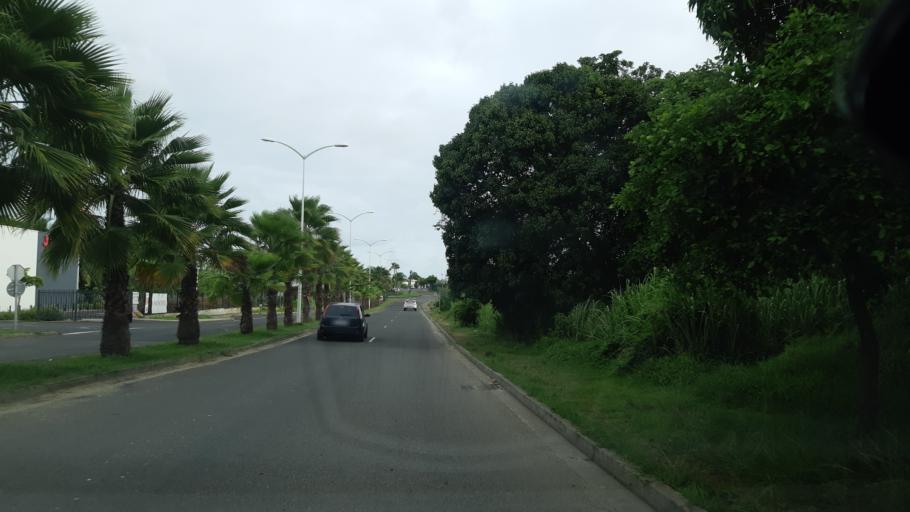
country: GP
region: Guadeloupe
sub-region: Guadeloupe
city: Les Abymes
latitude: 16.2716
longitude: -61.5175
